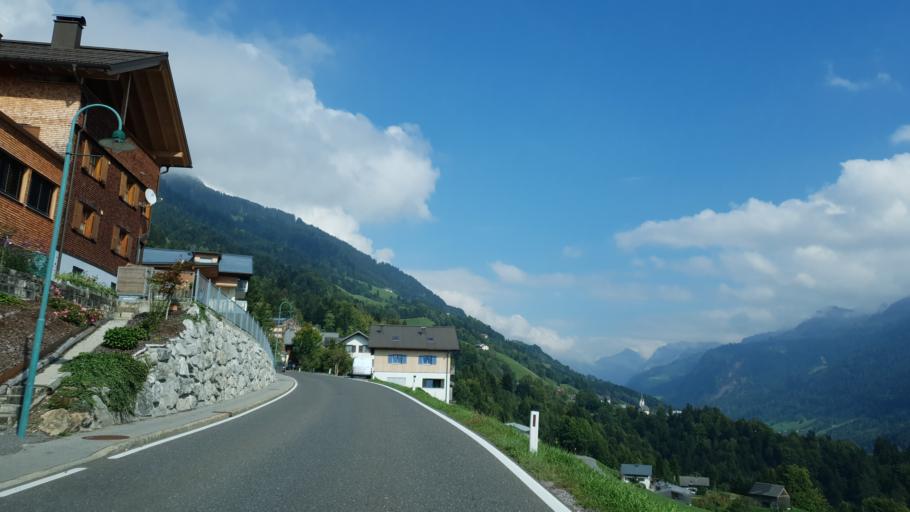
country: AT
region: Vorarlberg
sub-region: Politischer Bezirk Bludenz
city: Blons
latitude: 47.2213
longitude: 9.8202
